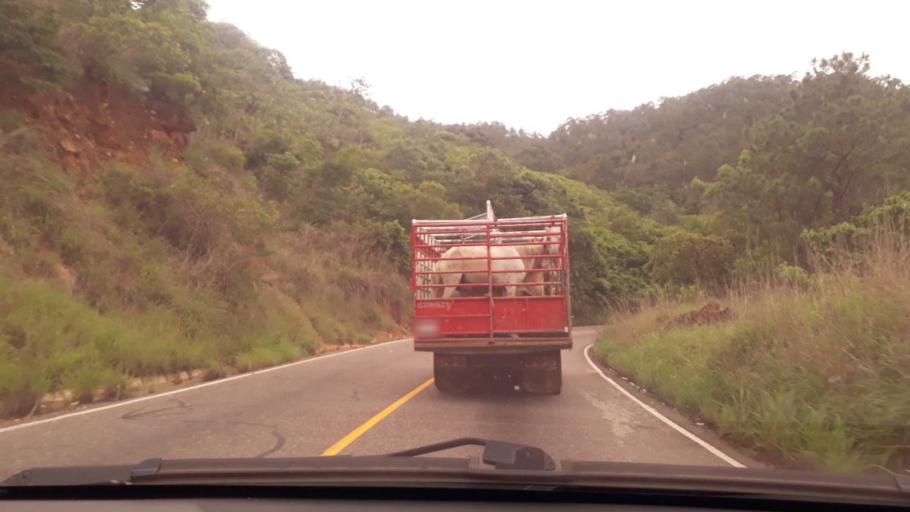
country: GT
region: Chiquimula
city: San Jose La Arada
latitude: 14.7098
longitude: -89.6158
